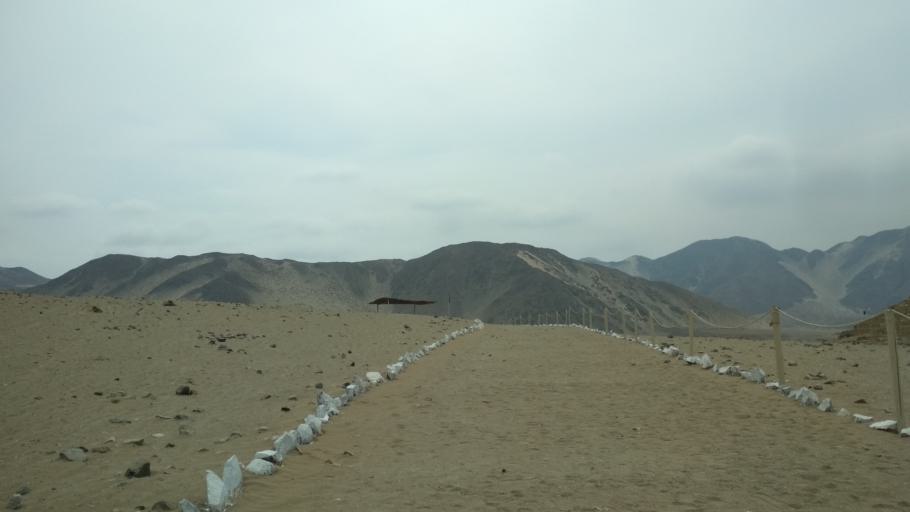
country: PE
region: Lima
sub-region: Huaura
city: Vegueta
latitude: -10.8935
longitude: -77.5179
